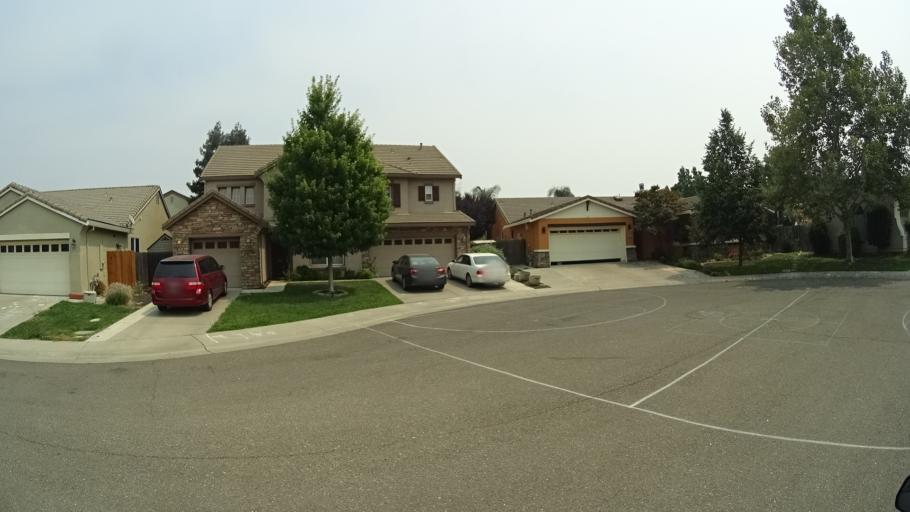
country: US
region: California
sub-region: Sacramento County
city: Laguna
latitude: 38.4001
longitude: -121.4391
